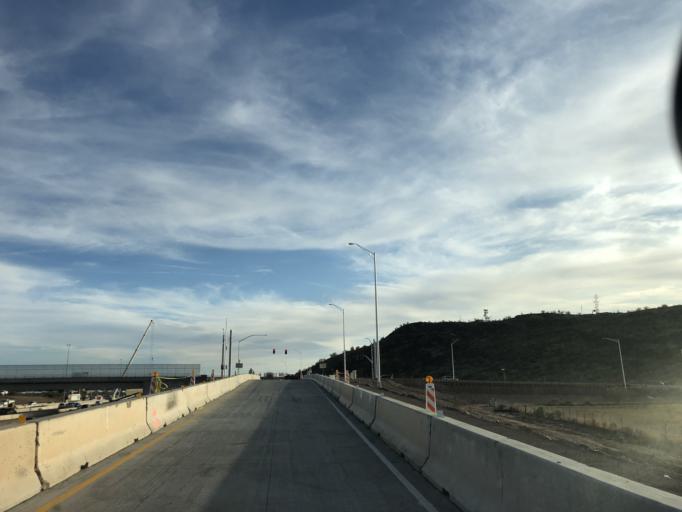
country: US
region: Arizona
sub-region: Maricopa County
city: Anthem
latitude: 33.7013
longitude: -112.1157
